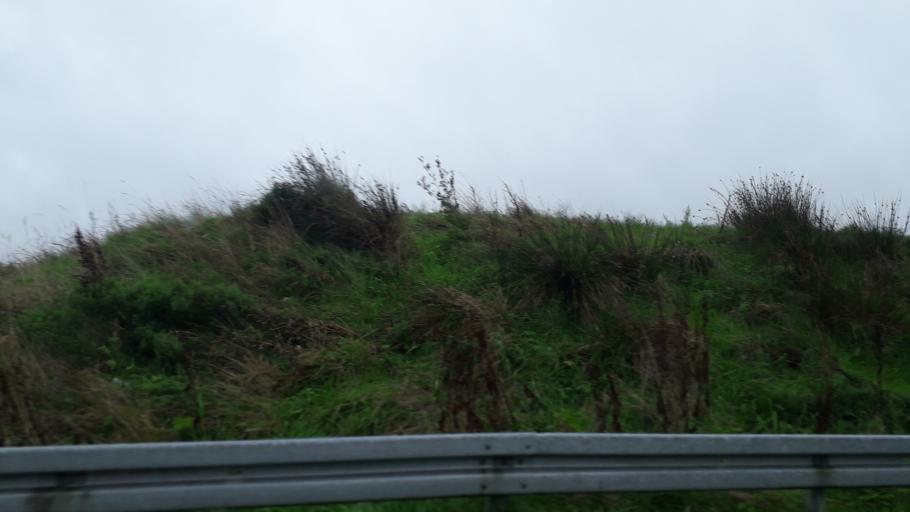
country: IE
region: Connaught
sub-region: Roscommon
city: Ballaghaderreen
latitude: 53.8887
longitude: -8.4953
